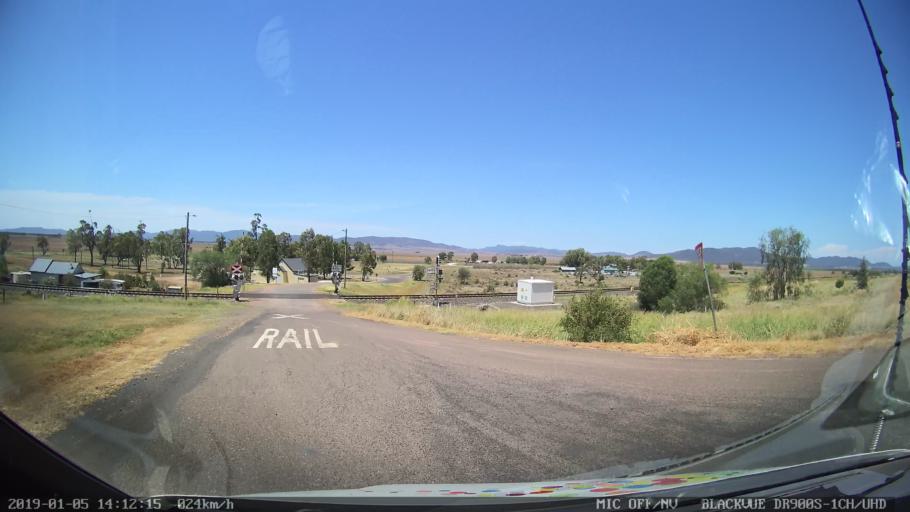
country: AU
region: New South Wales
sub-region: Liverpool Plains
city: Quirindi
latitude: -31.2479
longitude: 150.4670
